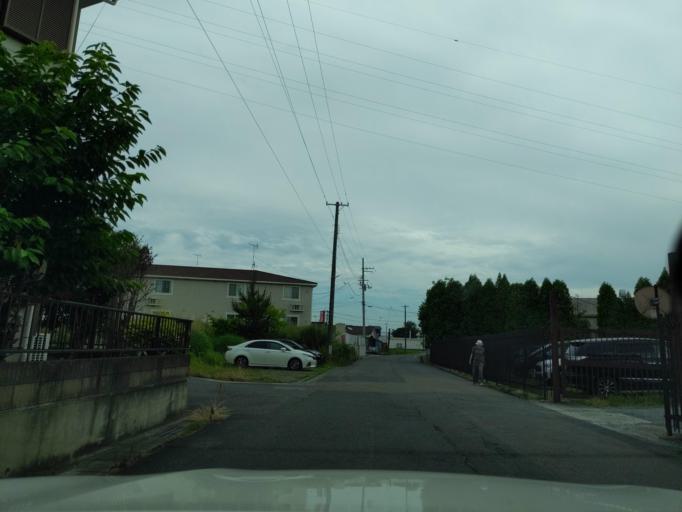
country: JP
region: Fukushima
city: Koriyama
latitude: 37.4199
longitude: 140.4025
